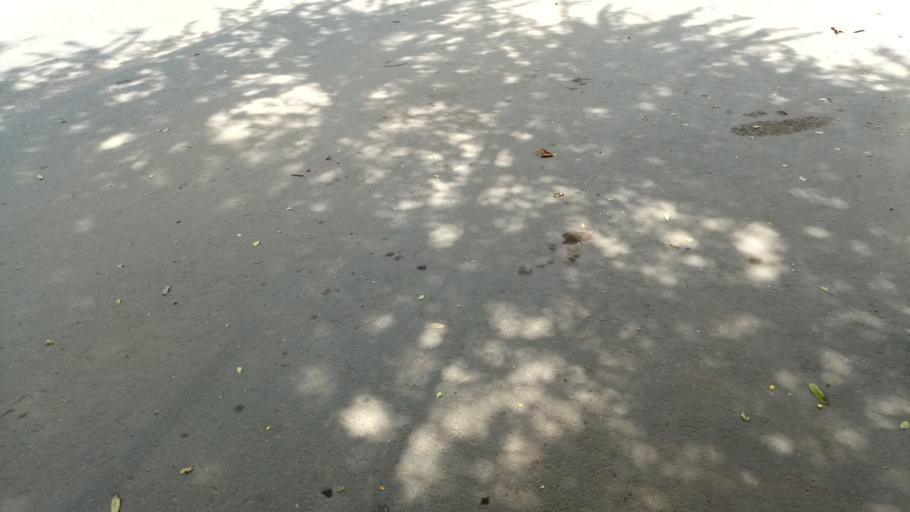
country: GH
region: Central
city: Cape Coast
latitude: 5.1304
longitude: -1.2901
